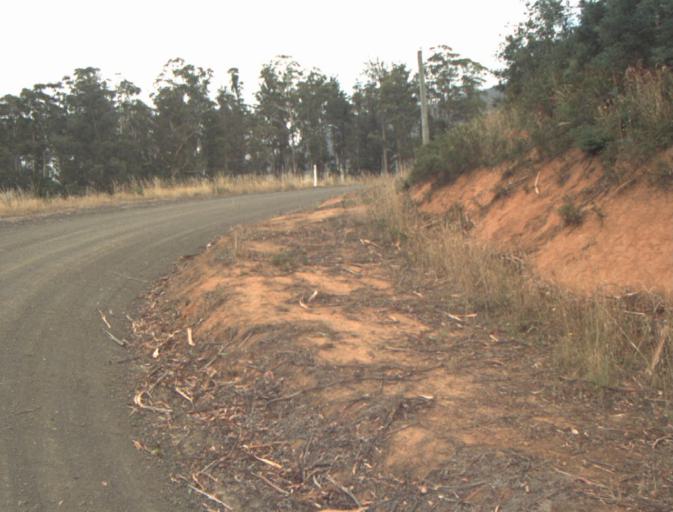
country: AU
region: Tasmania
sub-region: Northern Midlands
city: Evandale
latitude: -41.4588
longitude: 147.4607
